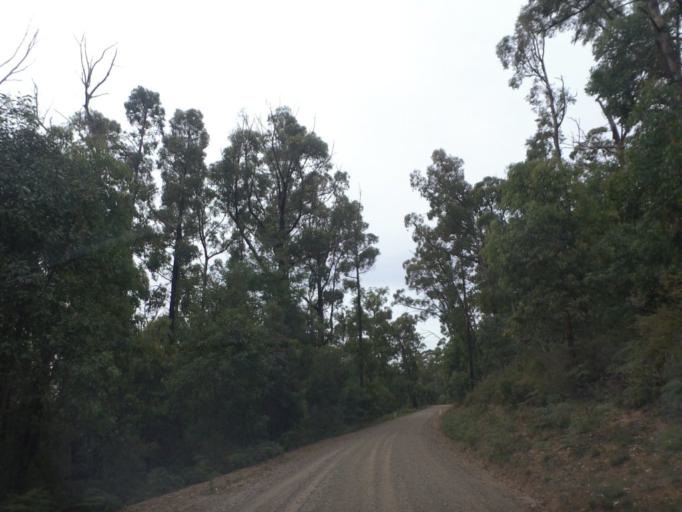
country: AU
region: Victoria
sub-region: Yarra Ranges
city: Healesville
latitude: -37.4251
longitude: 145.5809
